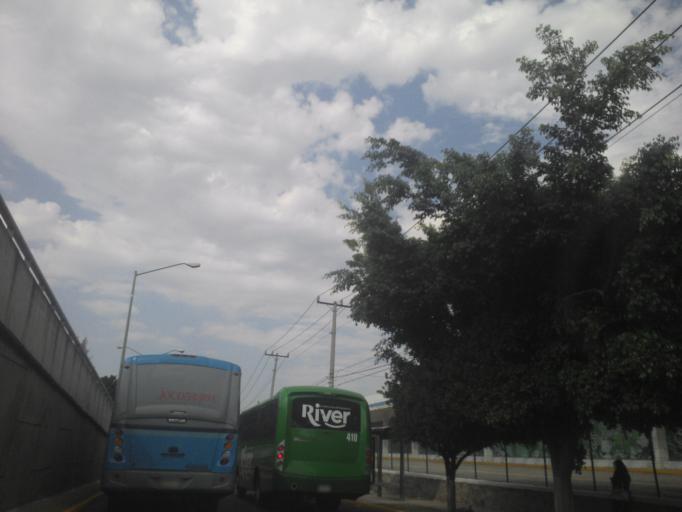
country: MX
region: Jalisco
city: Guadalajara
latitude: 20.6604
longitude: -103.3822
